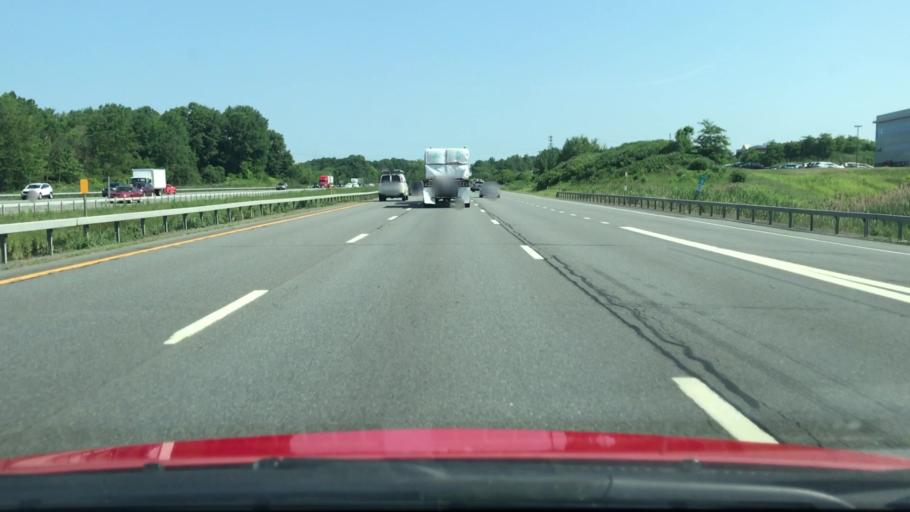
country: US
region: New York
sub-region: Albany County
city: Cohoes
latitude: 42.7671
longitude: -73.7617
